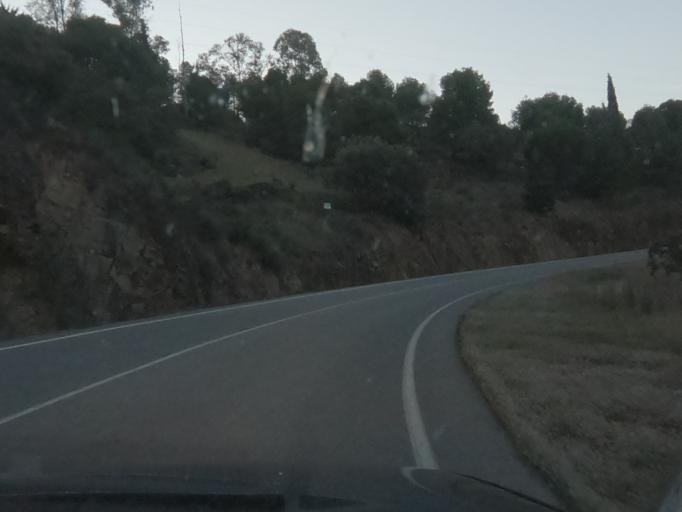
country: ES
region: Extremadura
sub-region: Provincia de Caceres
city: Alcantara
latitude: 39.7298
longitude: -6.8950
